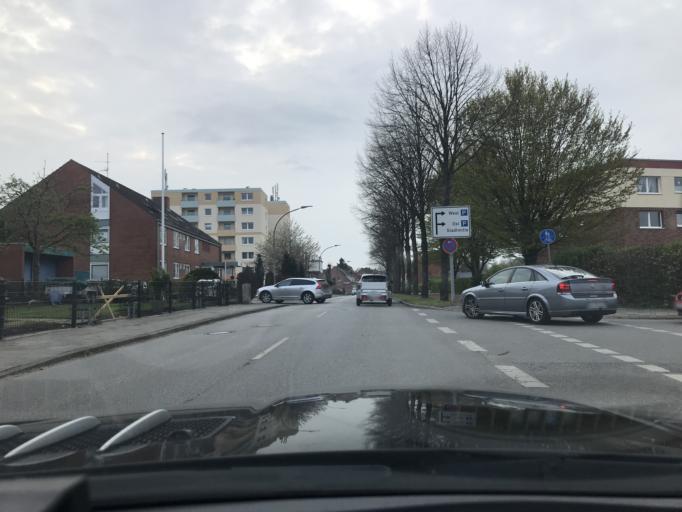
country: DE
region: Schleswig-Holstein
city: Burg auf Fehmarn
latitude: 54.4351
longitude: 11.2048
